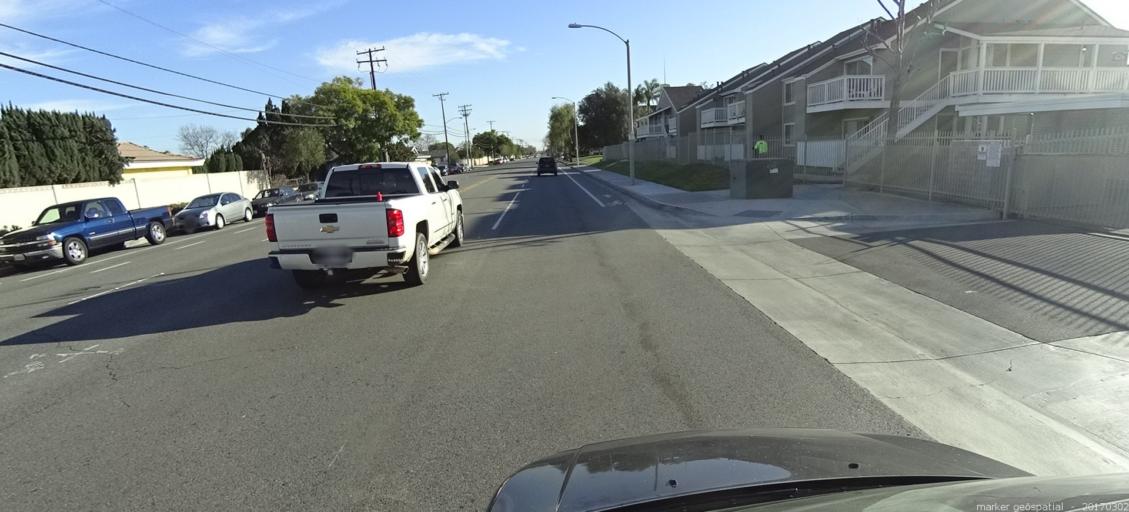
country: US
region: California
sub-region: Orange County
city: Placentia
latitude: 33.8362
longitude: -117.8718
